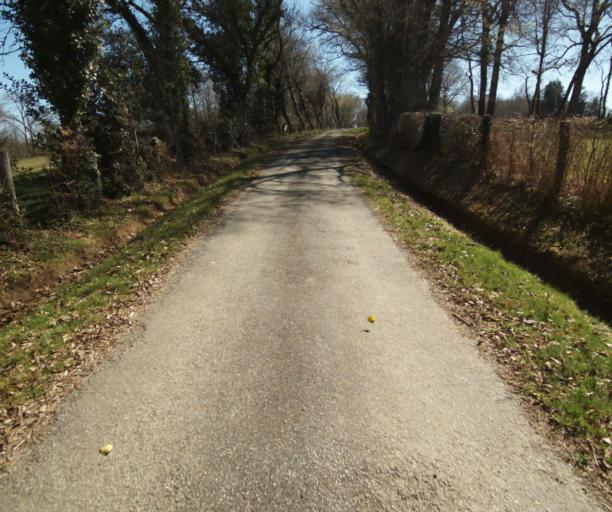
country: FR
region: Limousin
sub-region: Departement de la Correze
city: Chamboulive
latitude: 45.4018
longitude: 1.6794
